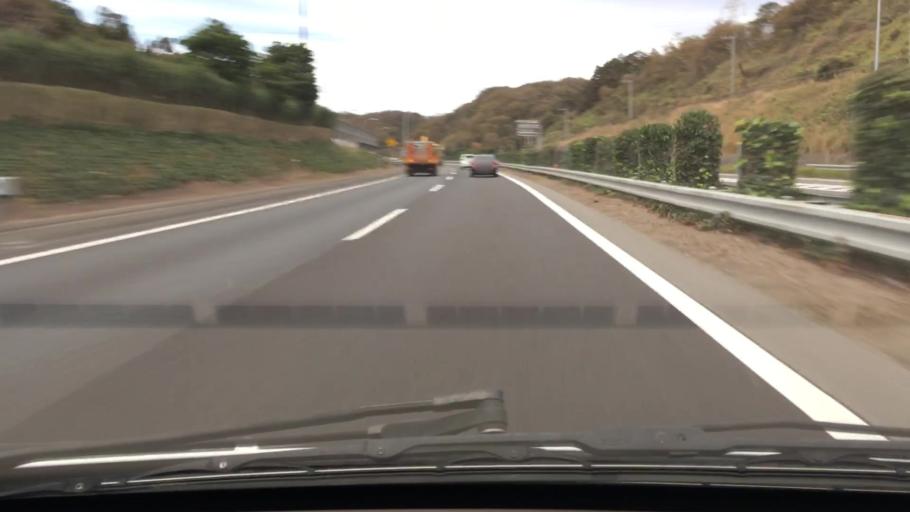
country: JP
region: Chiba
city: Ichihara
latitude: 35.4607
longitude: 140.0856
